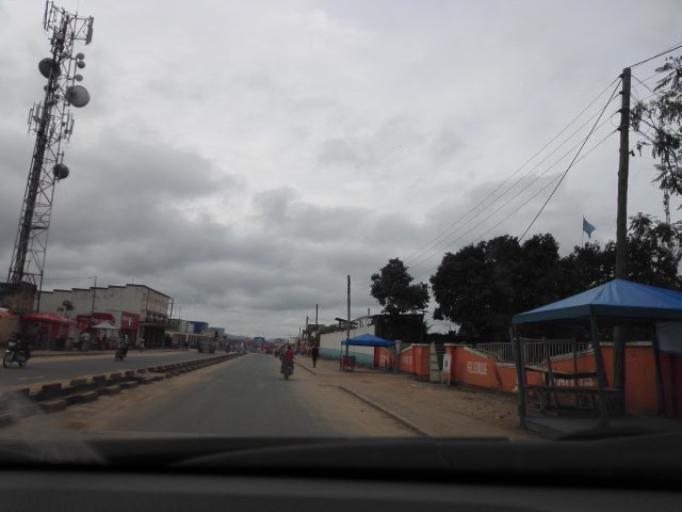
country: CD
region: Eastern Province
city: Bunia
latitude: 1.5543
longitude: 30.2478
